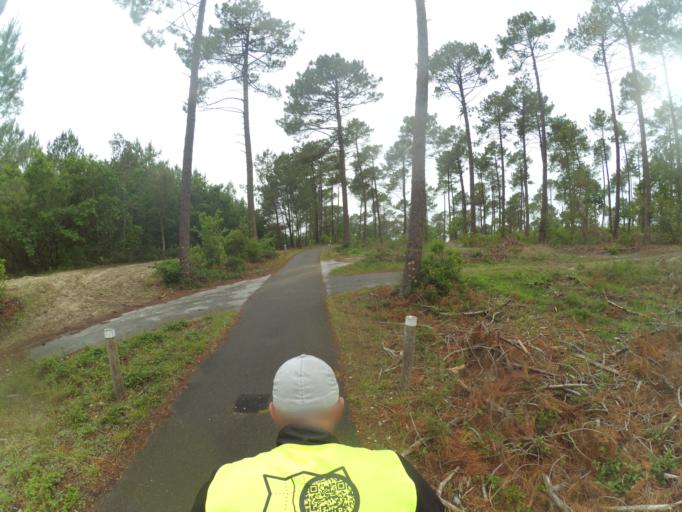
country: FR
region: Aquitaine
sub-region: Departement des Landes
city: Mimizan
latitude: 44.2185
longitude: -1.2495
